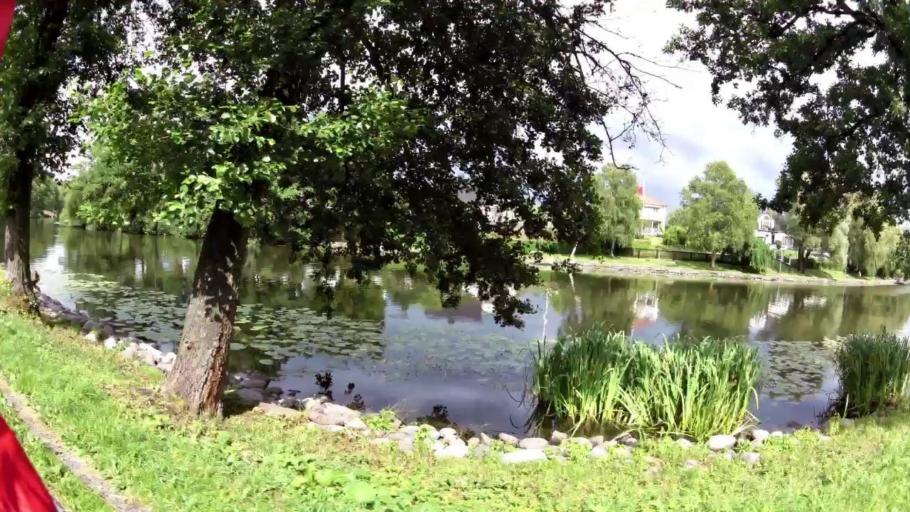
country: SE
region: OEstergoetland
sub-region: Linkopings Kommun
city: Linkoping
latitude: 58.4053
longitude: 15.6358
